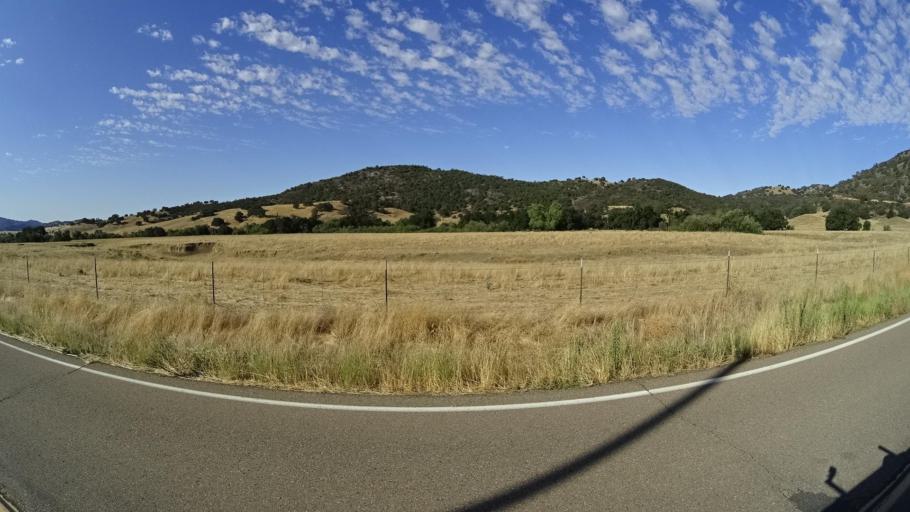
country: US
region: California
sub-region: San Diego County
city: Julian
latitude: 33.1458
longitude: -116.6886
